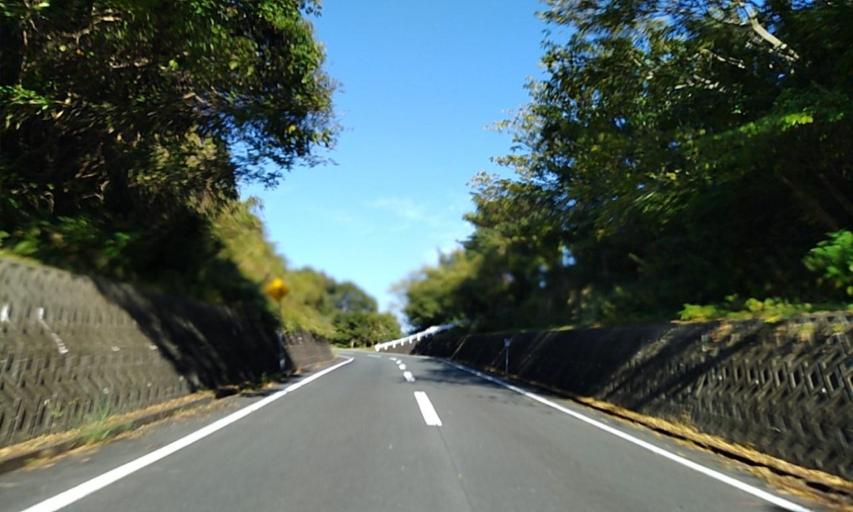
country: JP
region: Shizuoka
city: Hamakita
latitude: 34.8173
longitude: 137.6513
